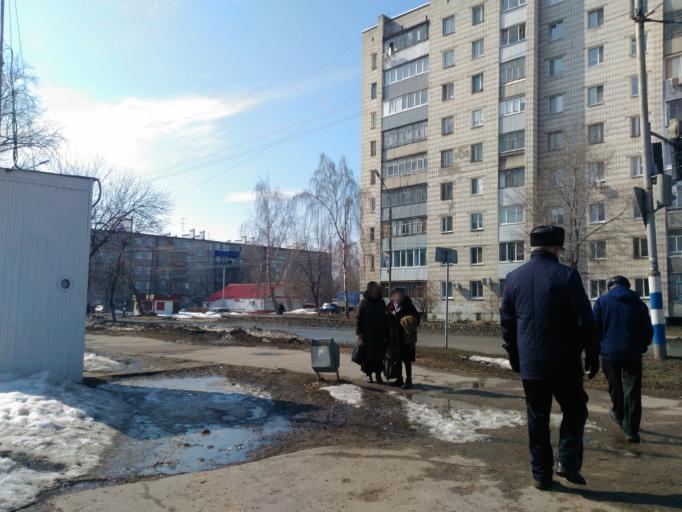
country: RU
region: Ulyanovsk
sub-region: Ulyanovskiy Rayon
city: Ulyanovsk
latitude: 54.3329
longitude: 48.4859
